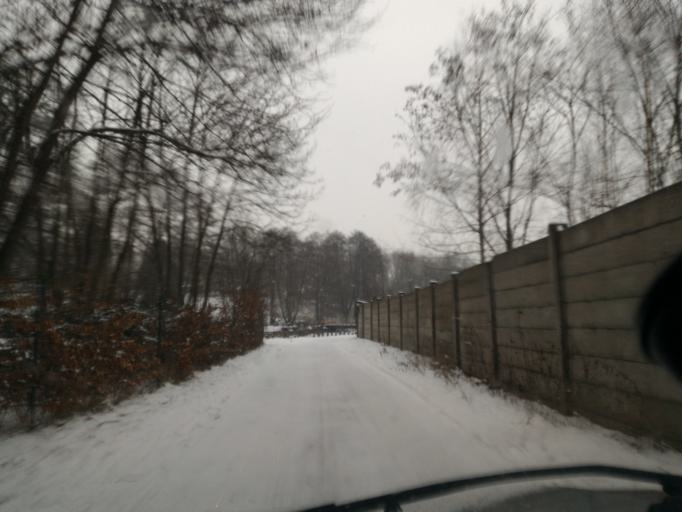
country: CZ
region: Ustecky
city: Varnsdorf
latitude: 50.9094
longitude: 14.6418
